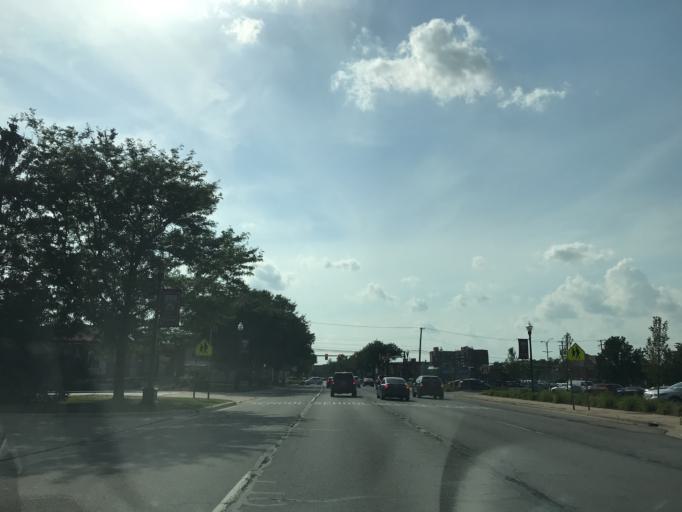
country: US
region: Michigan
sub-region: Wayne County
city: Wayne
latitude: 42.2815
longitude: -83.3795
